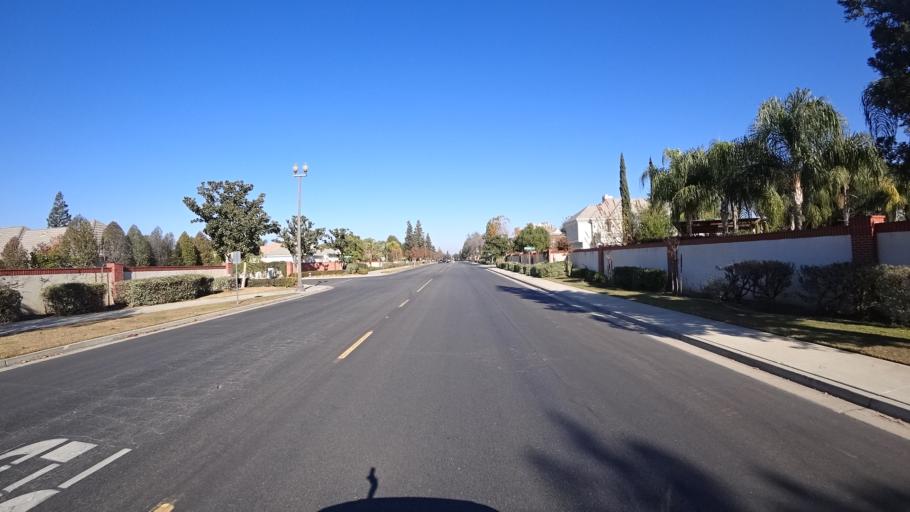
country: US
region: California
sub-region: Kern County
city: Greenacres
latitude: 35.3349
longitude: -119.1237
